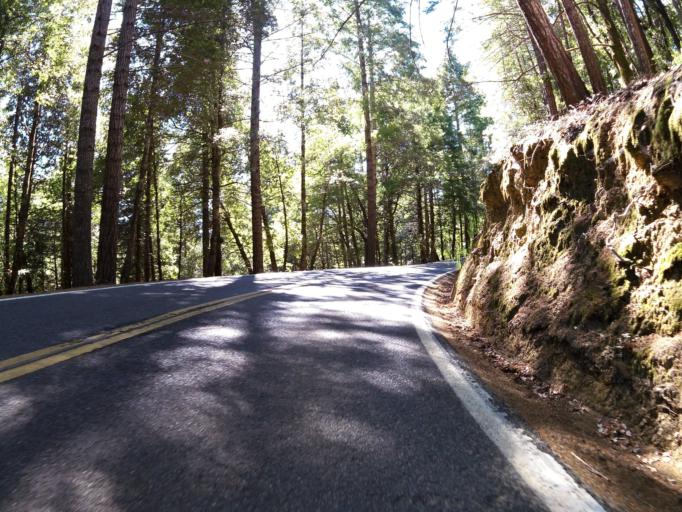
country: US
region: California
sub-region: Humboldt County
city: Redway
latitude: 39.8331
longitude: -123.7749
